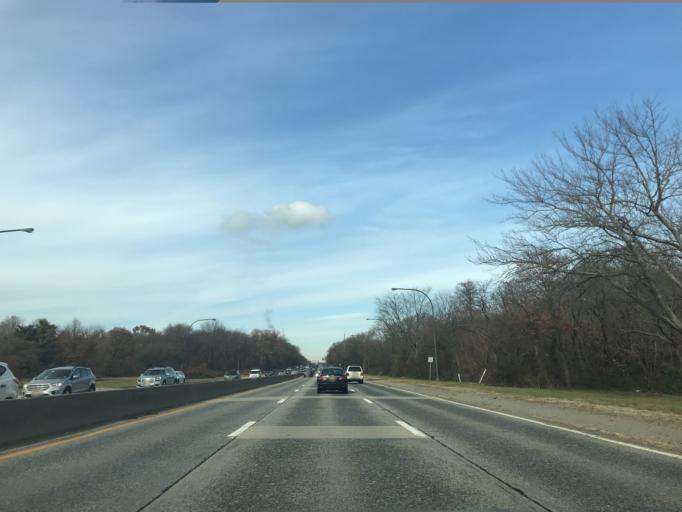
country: US
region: New York
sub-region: Nassau County
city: Uniondale
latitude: 40.7070
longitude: -73.5785
